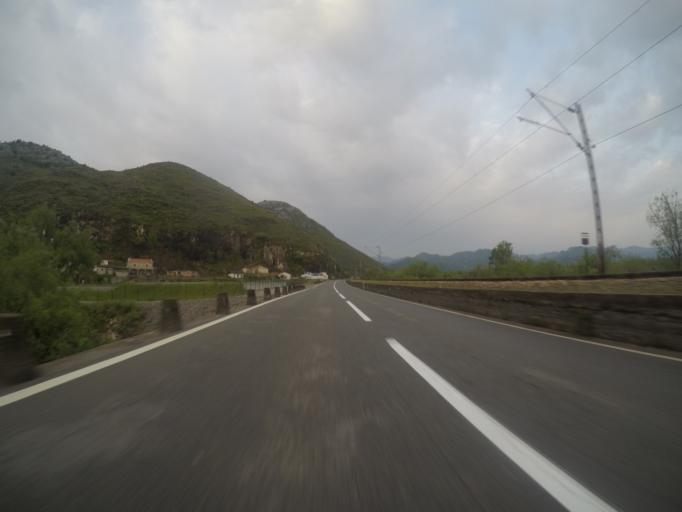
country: ME
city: Mojanovici
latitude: 42.2820
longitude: 19.1390
